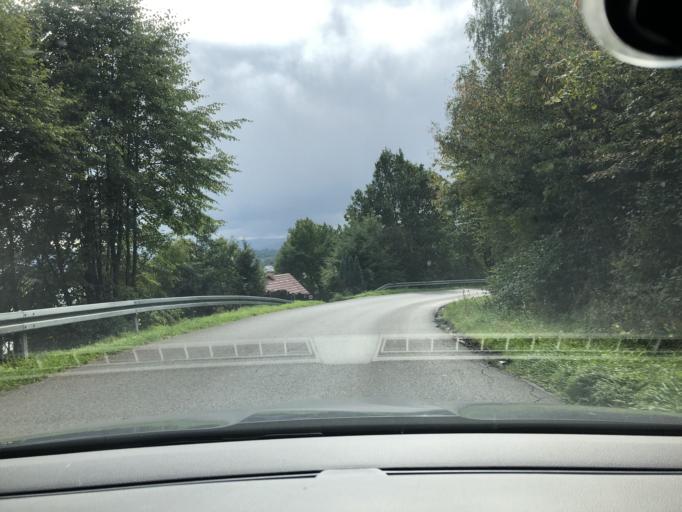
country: PL
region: Silesian Voivodeship
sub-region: Powiat zywiecki
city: Czernichow
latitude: 49.7351
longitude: 19.2081
